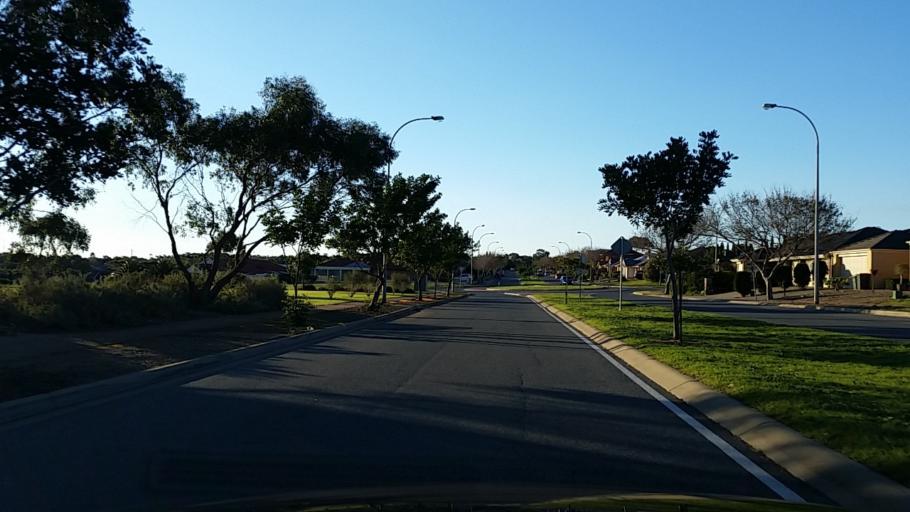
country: AU
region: South Australia
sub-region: Onkaparinga
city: Moana
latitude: -35.2056
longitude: 138.4833
